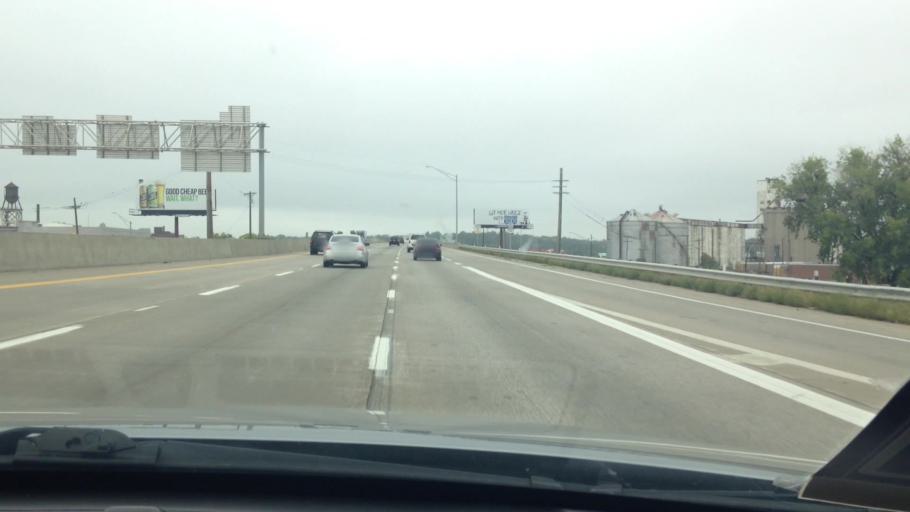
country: US
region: Missouri
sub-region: Clay County
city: North Kansas City
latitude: 39.1293
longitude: -94.5679
